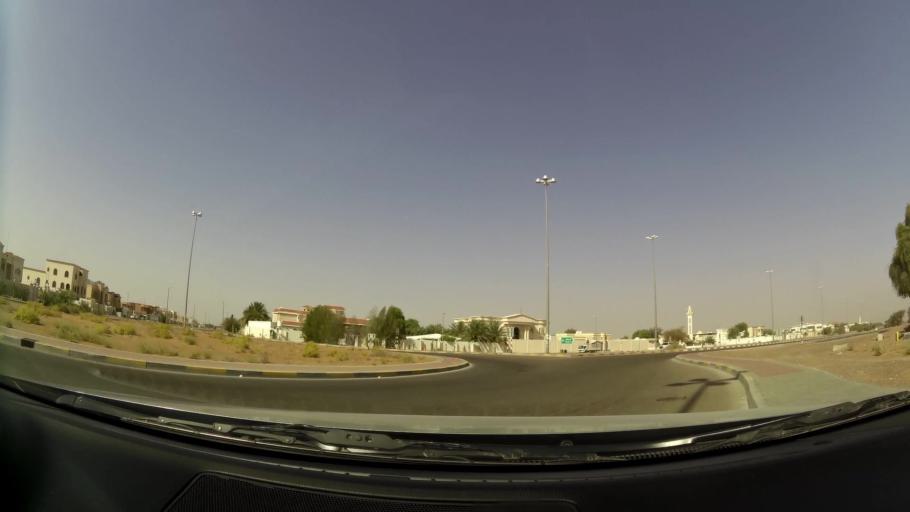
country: OM
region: Al Buraimi
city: Al Buraymi
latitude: 24.3411
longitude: 55.8008
